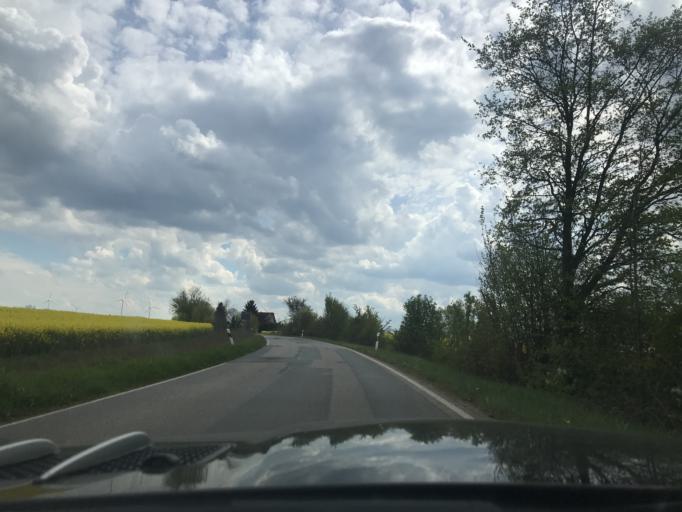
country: DE
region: Schleswig-Holstein
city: Timmendorfer Strand
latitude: 53.9559
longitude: 10.7896
